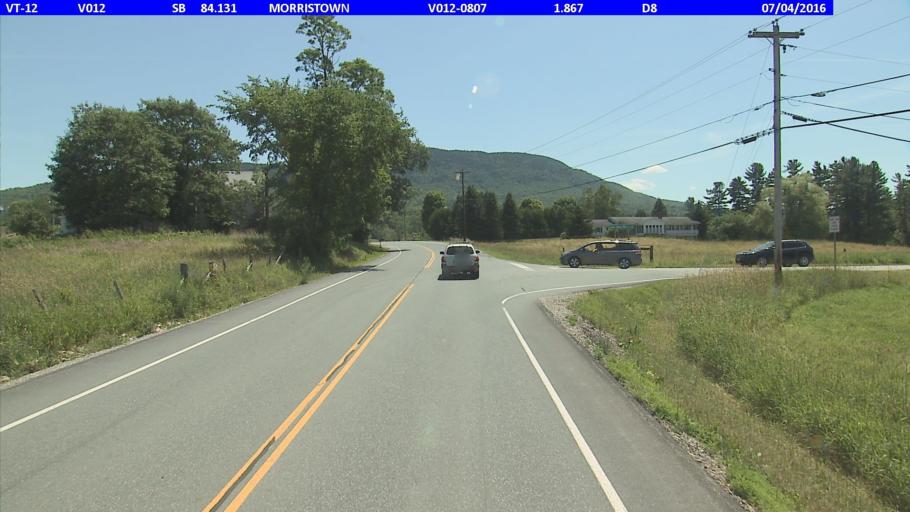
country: US
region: Vermont
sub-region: Lamoille County
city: Morrisville
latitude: 44.5511
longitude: -72.5734
